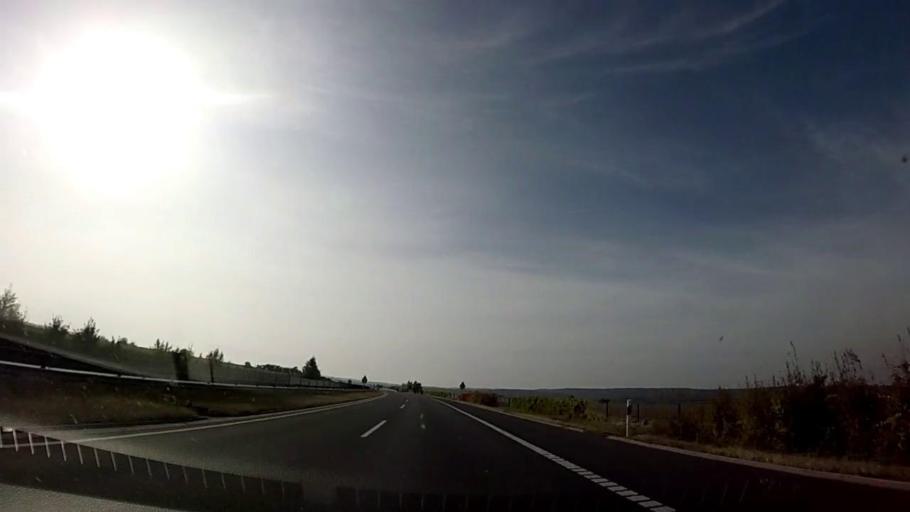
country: HU
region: Somogy
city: Zamardi
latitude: 46.8746
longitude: 17.9676
